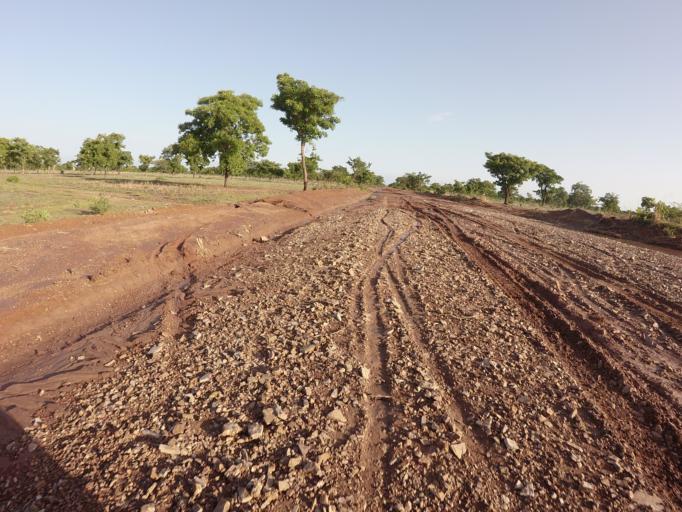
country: TG
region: Savanes
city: Sansanne-Mango
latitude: 10.3653
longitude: -0.0937
